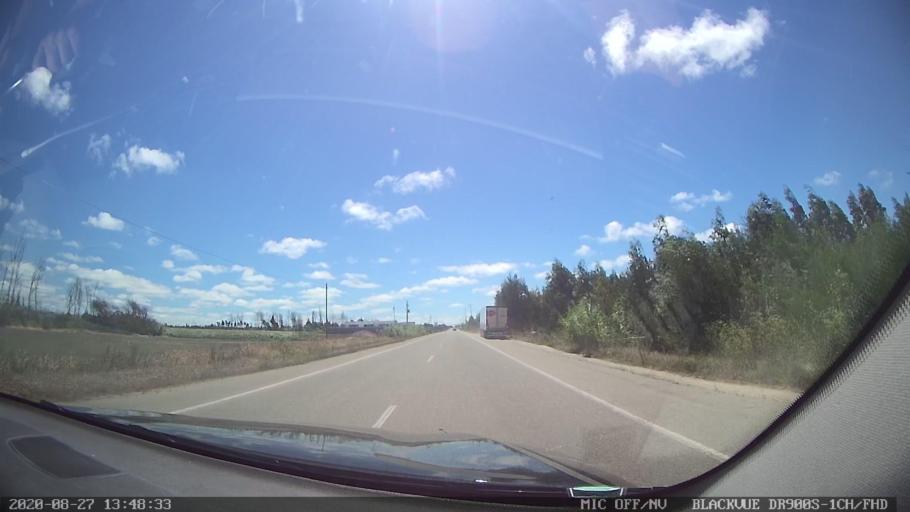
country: PT
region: Coimbra
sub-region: Mira
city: Mira
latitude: 40.3763
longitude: -8.7452
